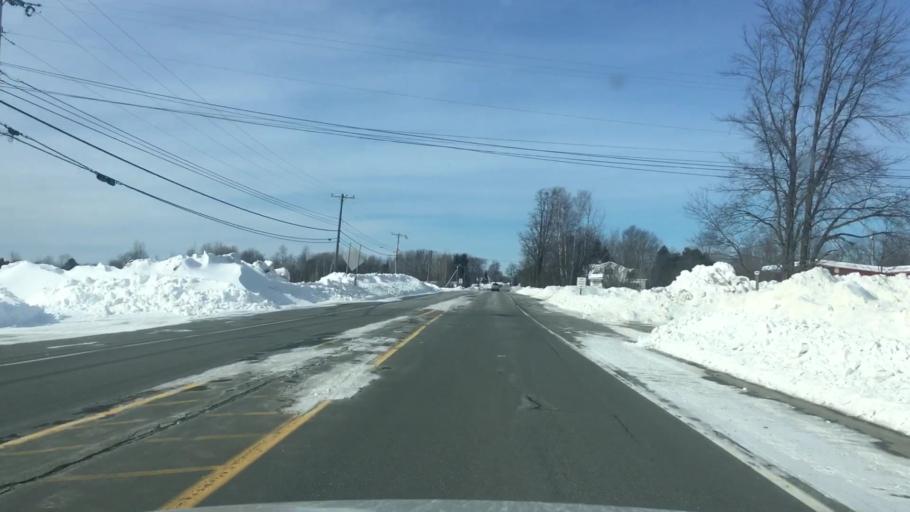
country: US
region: Maine
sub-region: Penobscot County
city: Charleston
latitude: 45.0179
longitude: -69.0282
